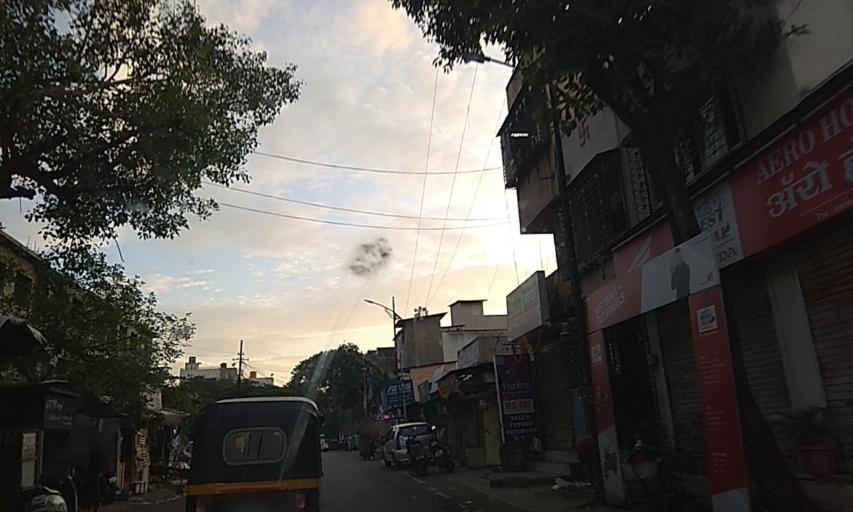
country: IN
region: Maharashtra
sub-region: Pune Division
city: Pune
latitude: 18.4943
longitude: 73.8506
